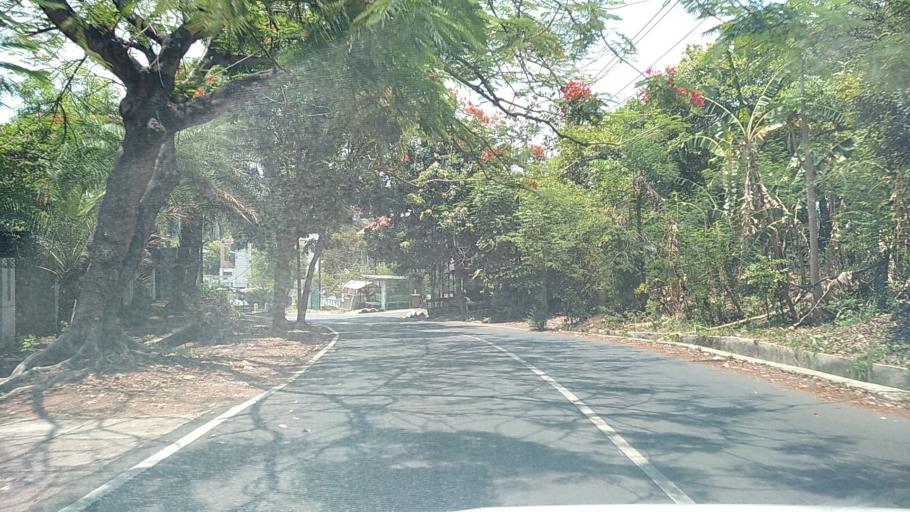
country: ID
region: Central Java
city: Semarang
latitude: -7.0251
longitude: 110.4166
